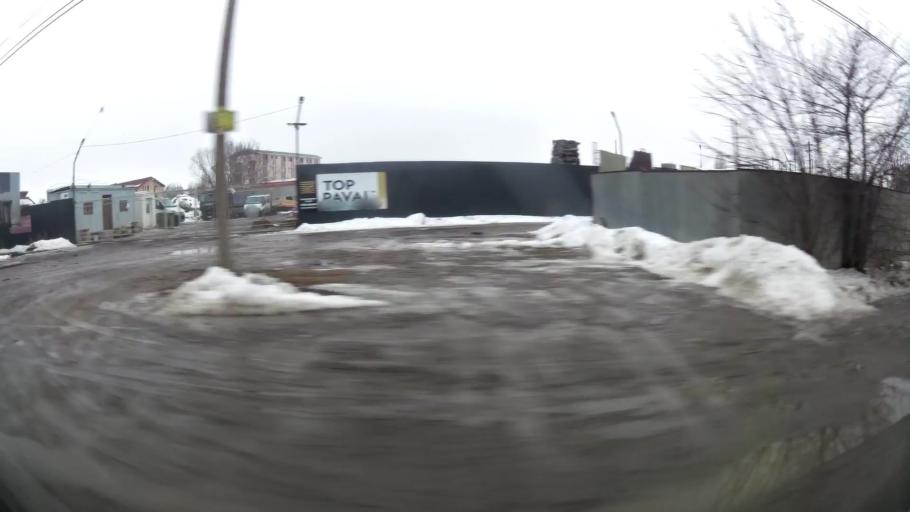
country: RO
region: Ilfov
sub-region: Comuna Bragadiru
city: Bragadiru
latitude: 44.3844
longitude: 25.9914
